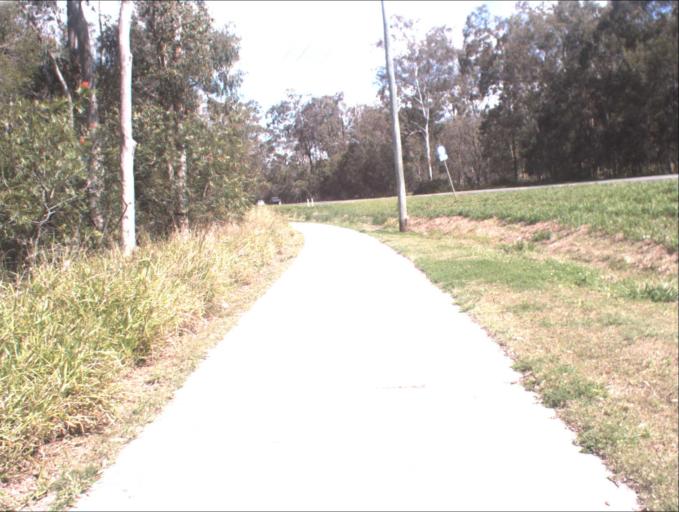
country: AU
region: Queensland
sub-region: Logan
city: Park Ridge South
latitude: -27.7395
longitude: 153.0268
